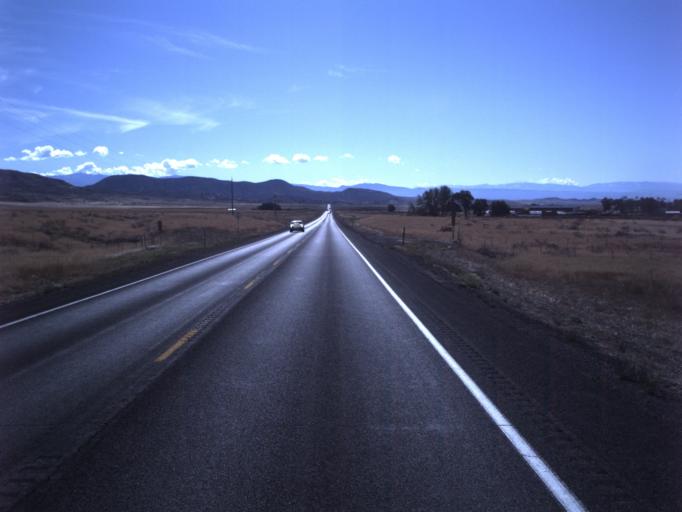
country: US
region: Utah
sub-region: Sanpete County
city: Gunnison
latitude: 39.2719
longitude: -111.8731
